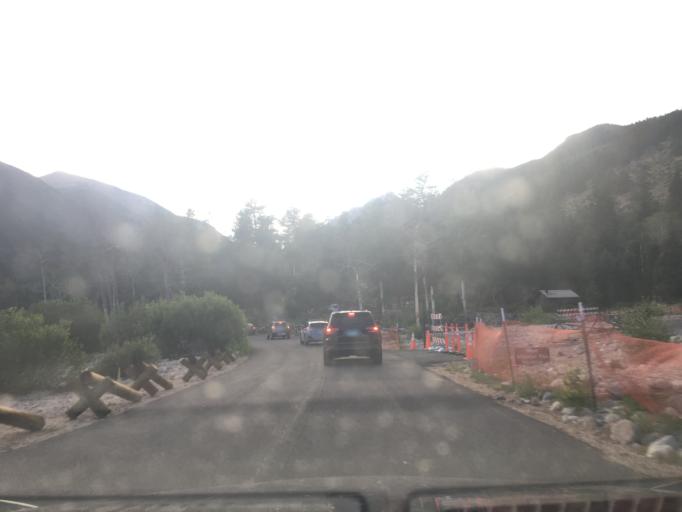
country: US
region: Colorado
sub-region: Larimer County
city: Estes Park
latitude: 40.4102
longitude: -105.6367
